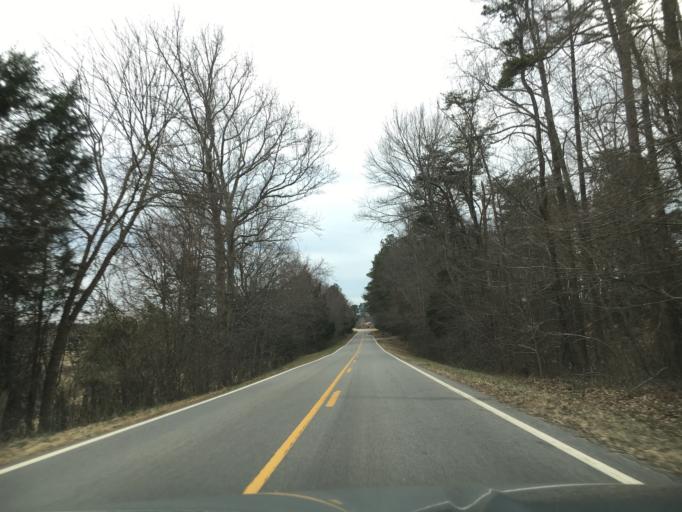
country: US
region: Virginia
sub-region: Charlotte County
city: Charlotte Court House
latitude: 37.0059
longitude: -78.6982
